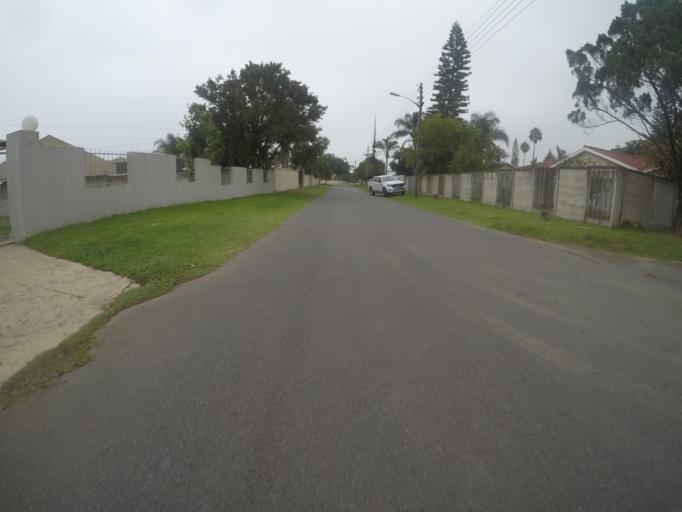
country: ZA
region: Eastern Cape
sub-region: Buffalo City Metropolitan Municipality
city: East London
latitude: -32.9457
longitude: 28.0037
